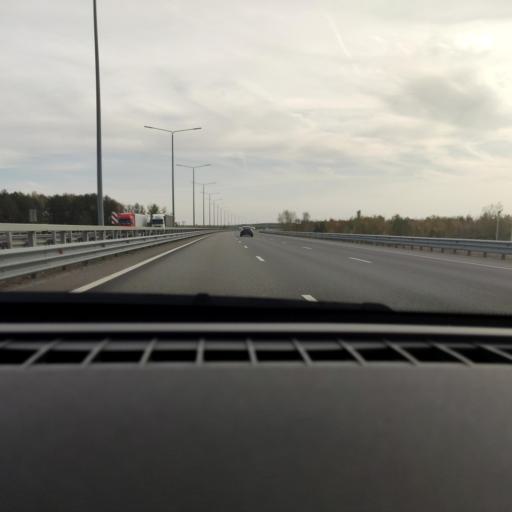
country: RU
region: Voronezj
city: Somovo
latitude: 51.7815
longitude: 39.2952
